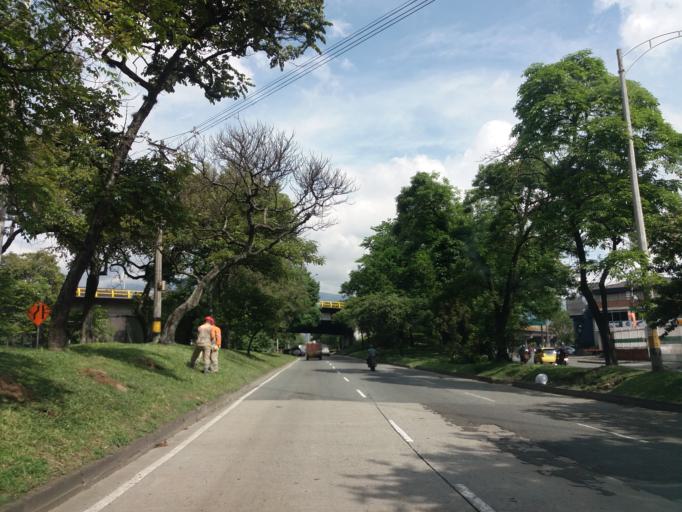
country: CO
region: Antioquia
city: Medellin
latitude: 6.2365
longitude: -75.5758
